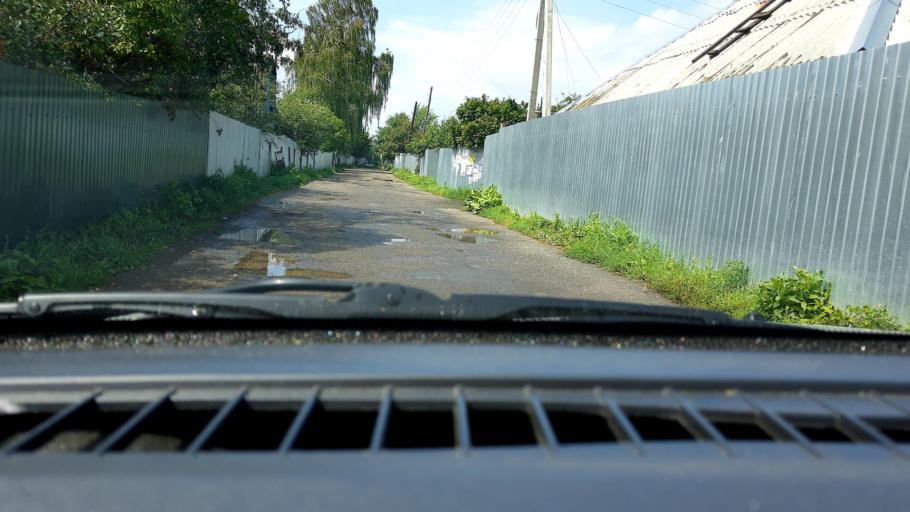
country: RU
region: Nizjnij Novgorod
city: Gorbatovka
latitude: 56.3830
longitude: 43.8227
